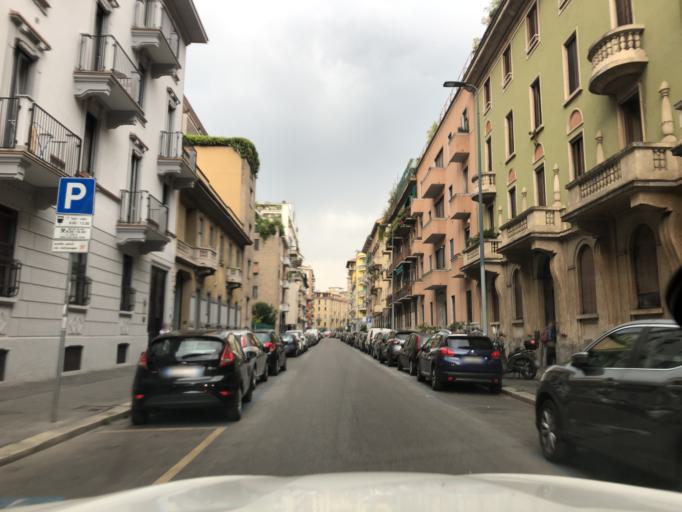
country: IT
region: Lombardy
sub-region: Citta metropolitana di Milano
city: Milano
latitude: 45.4897
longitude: 9.2114
